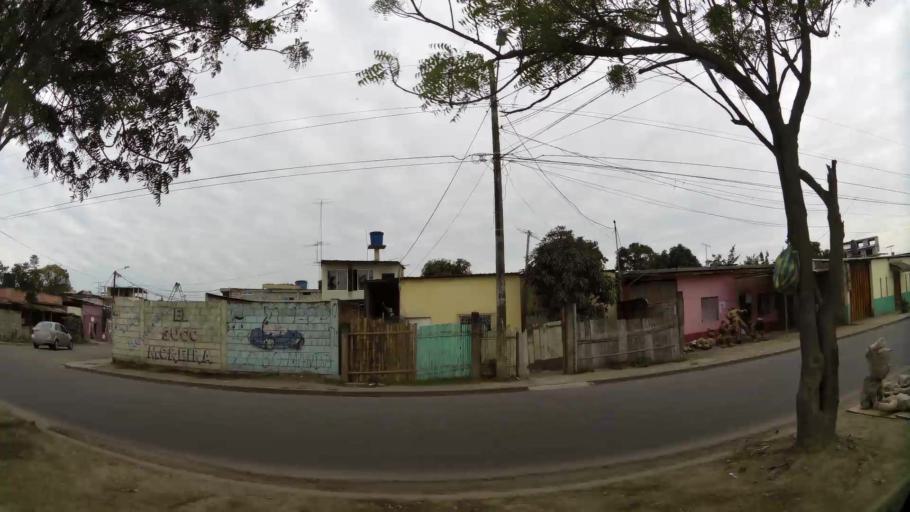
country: EC
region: El Oro
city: Machala
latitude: -3.2456
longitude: -79.9533
